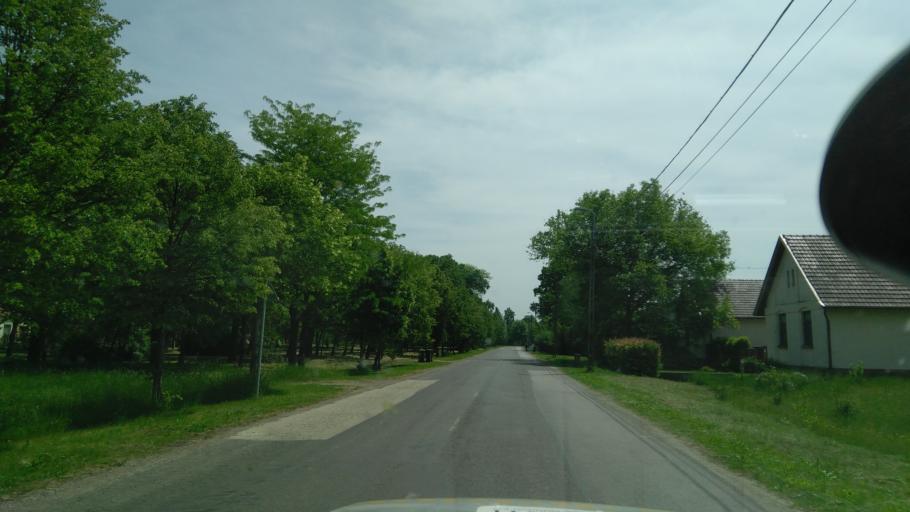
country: HU
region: Csongrad
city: Fabiansebestyen
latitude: 46.5869
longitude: 20.4726
